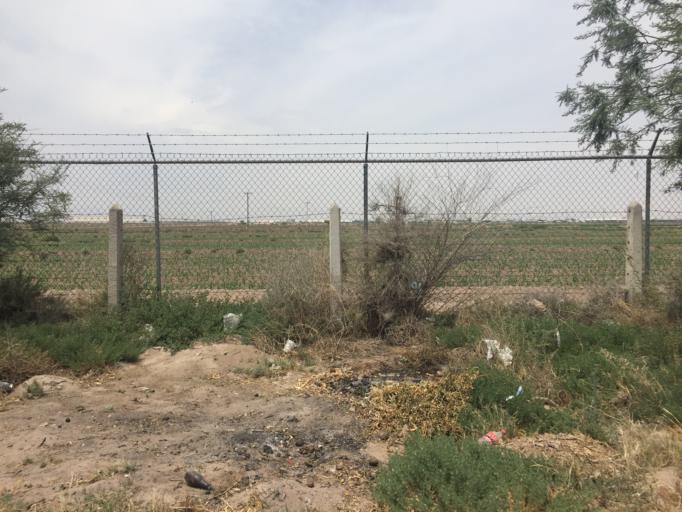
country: MX
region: Durango
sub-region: Gomez Palacio
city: San Jose de Vinedo
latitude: 25.6683
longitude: -103.4255
